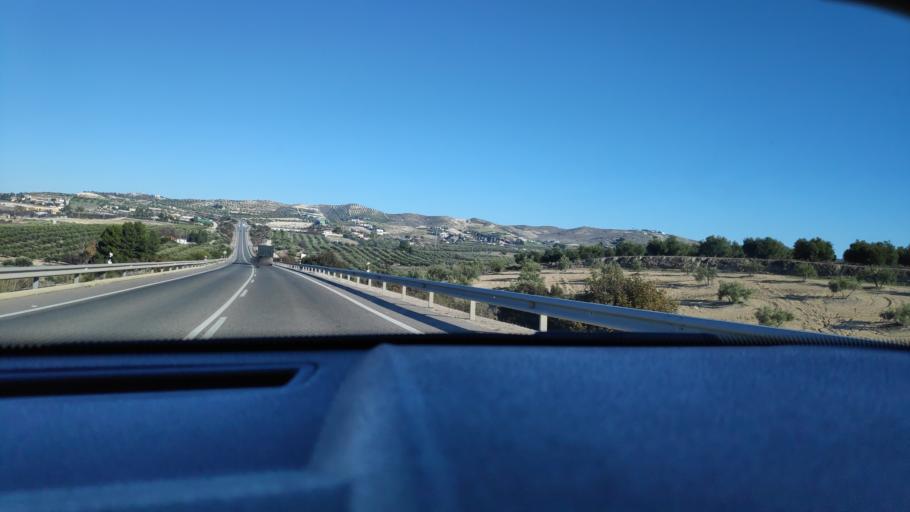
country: ES
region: Andalusia
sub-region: Province of Cordoba
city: Baena
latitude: 37.6115
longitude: -4.3008
